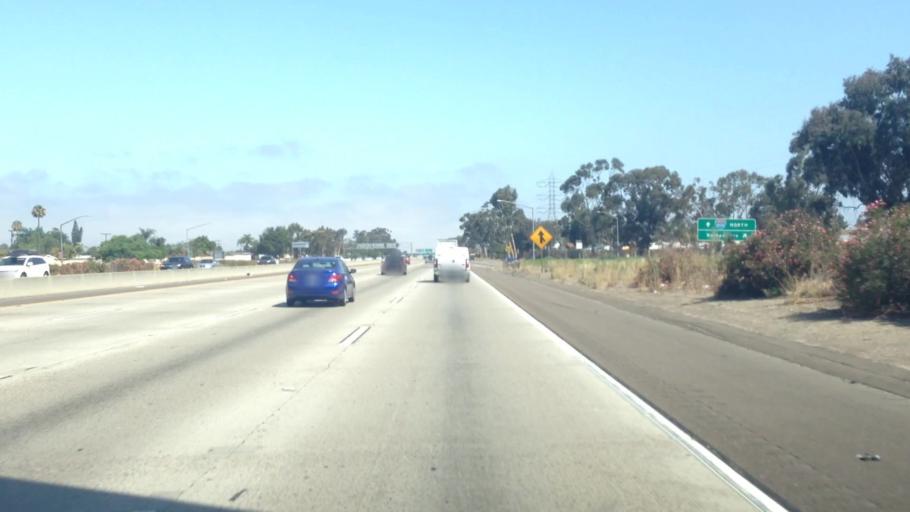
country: US
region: California
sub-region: San Diego County
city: San Diego
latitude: 32.8222
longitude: -117.1624
